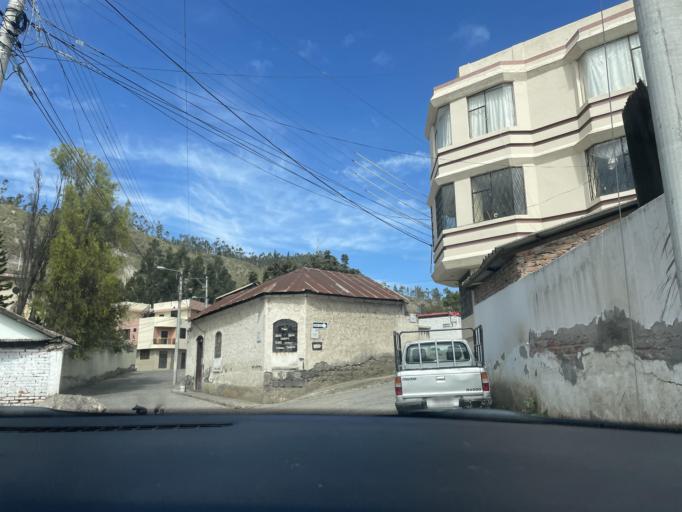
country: EC
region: Chimborazo
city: Guano
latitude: -1.6088
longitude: -78.6449
